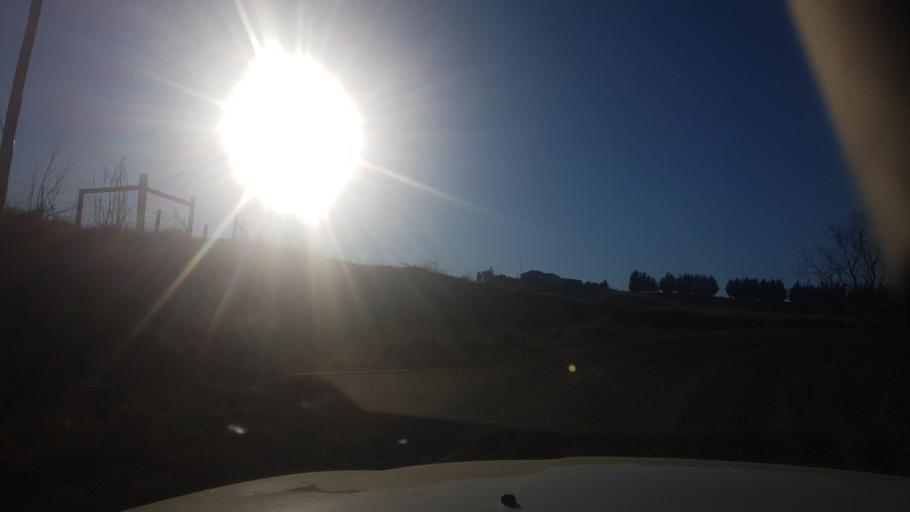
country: NZ
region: Canterbury
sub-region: Timaru District
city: Pleasant Point
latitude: -44.3433
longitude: 171.0698
